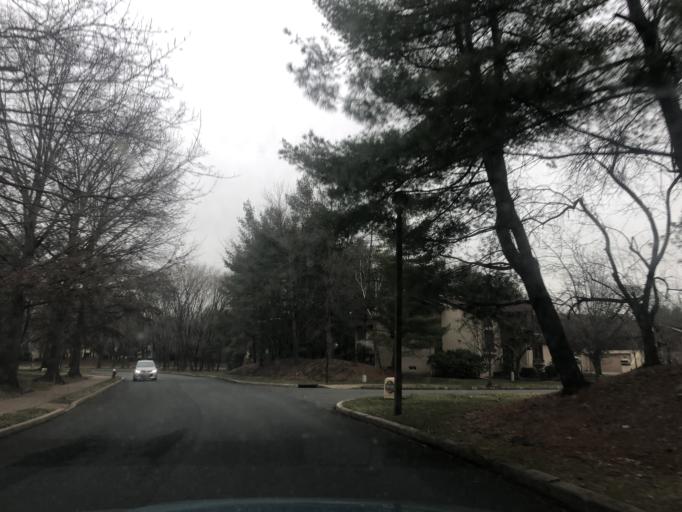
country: US
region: New Jersey
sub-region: Somerset County
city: Kingston
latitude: 40.3488
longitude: -74.6224
